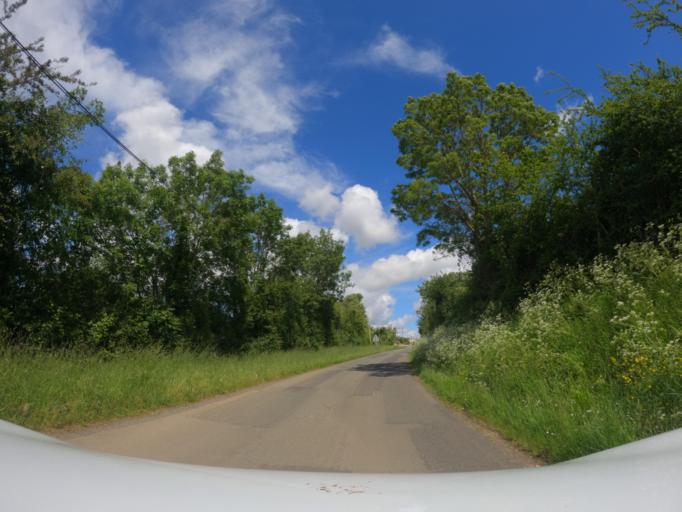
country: FR
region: Pays de la Loire
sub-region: Departement de la Vendee
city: Le Champ-Saint-Pere
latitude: 46.4910
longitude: -1.3330
